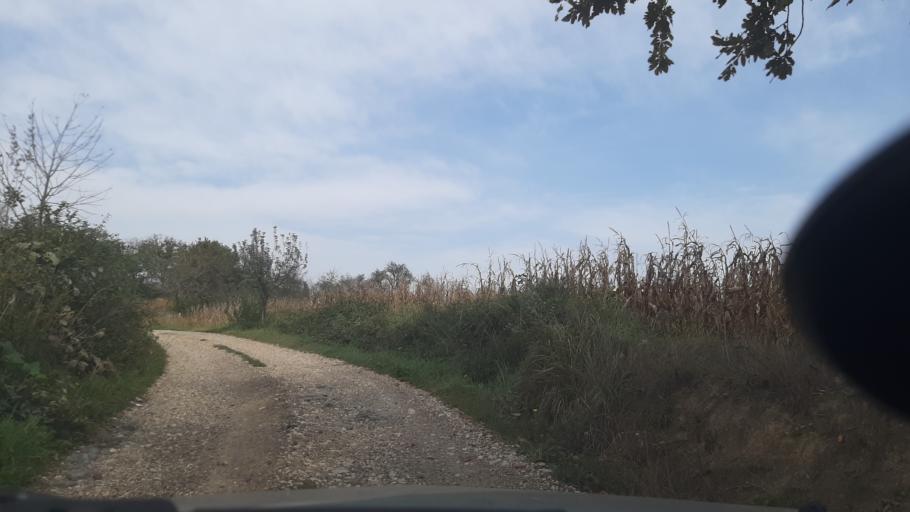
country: BA
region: Republika Srpska
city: Maglajani
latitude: 44.8760
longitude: 17.4727
